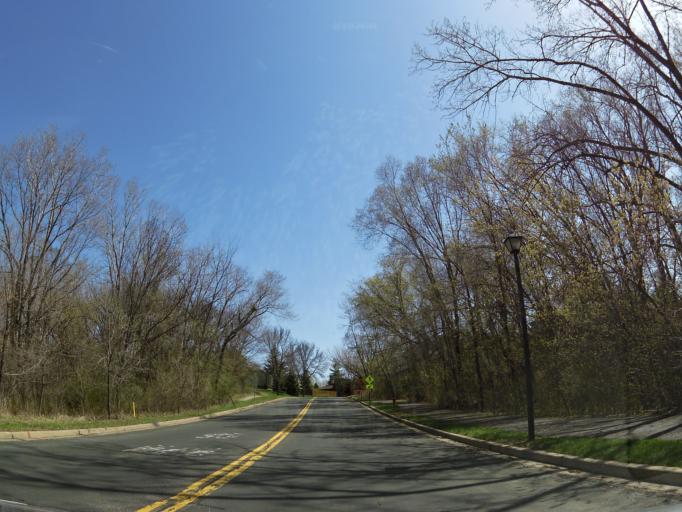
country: US
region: Wisconsin
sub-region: Saint Croix County
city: Hudson
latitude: 44.9701
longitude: -92.7350
